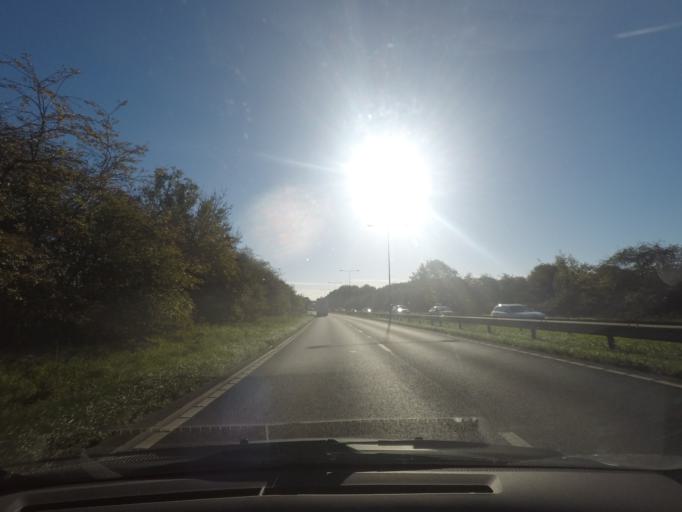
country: GB
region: England
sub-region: East Riding of Yorkshire
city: Welton
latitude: 53.7338
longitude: -0.5575
